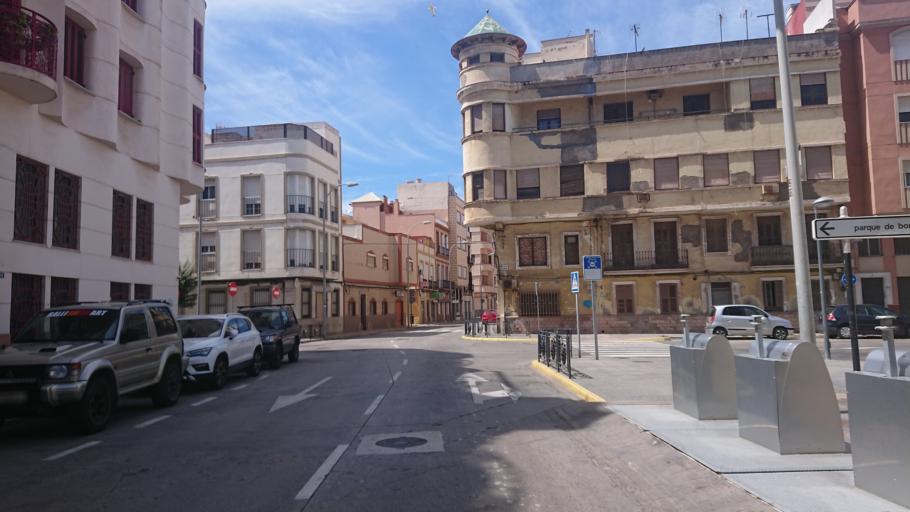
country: ES
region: Melilla
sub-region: Melilla
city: Melilla
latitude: 35.2902
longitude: -2.9401
